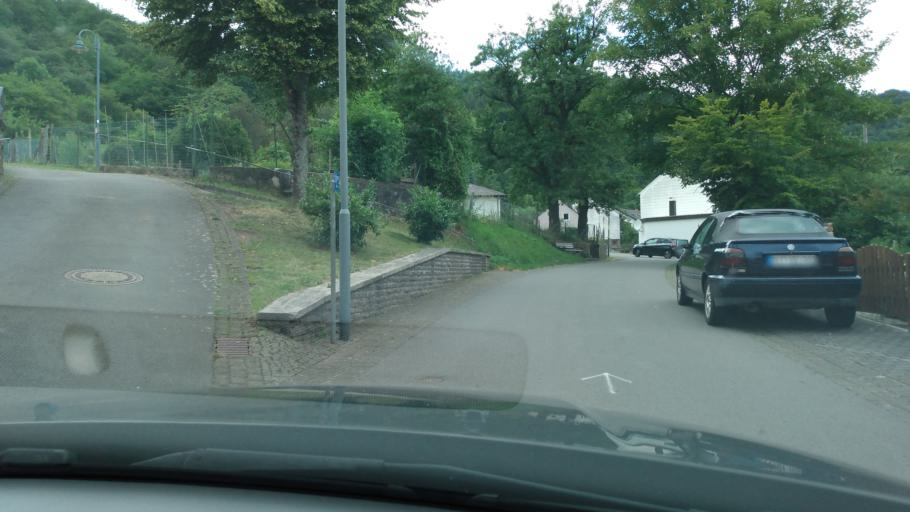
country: DE
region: Rheinland-Pfalz
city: Meerfeld
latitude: 50.0943
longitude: 6.7538
